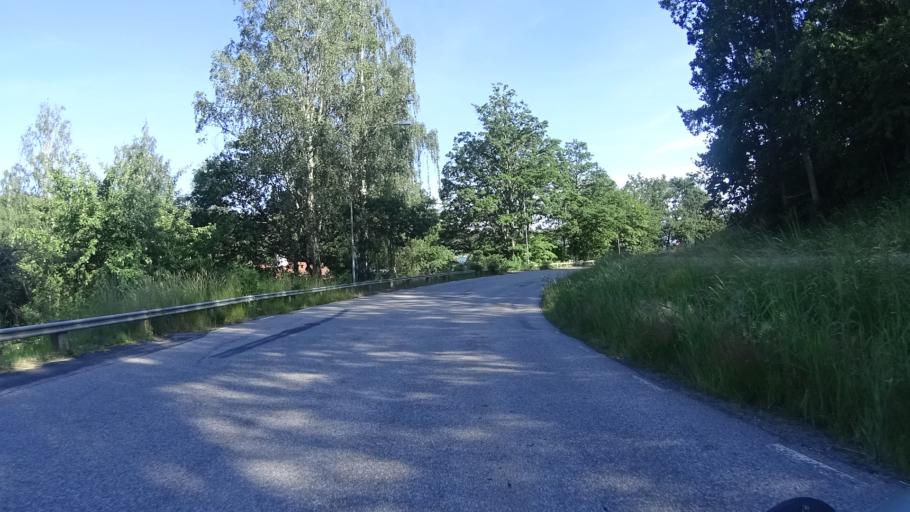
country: SE
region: Kalmar
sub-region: Vasterviks Kommun
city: Gamleby
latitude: 57.9040
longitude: 16.4136
